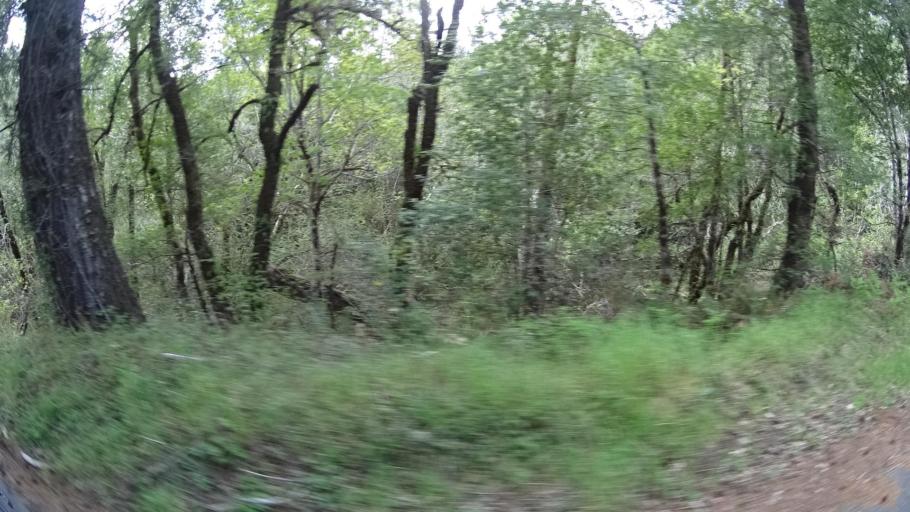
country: US
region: California
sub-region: Humboldt County
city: Redway
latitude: 40.0131
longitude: -123.9329
